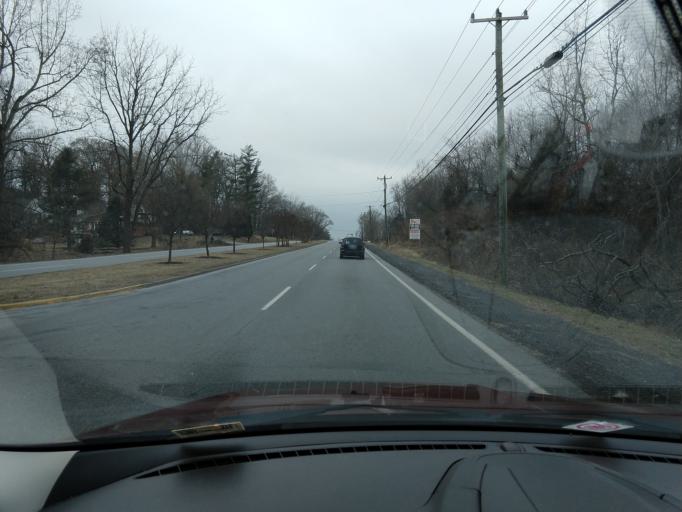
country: US
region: Virginia
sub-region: City of Waynesboro
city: Waynesboro
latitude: 38.0677
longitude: -78.9239
